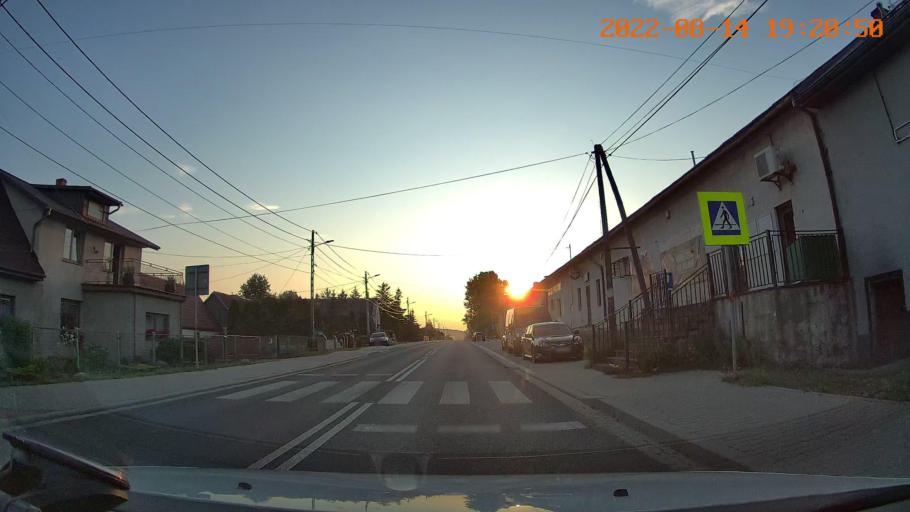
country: PL
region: Swietokrzyskie
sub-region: Powiat kielecki
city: Piekoszow
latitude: 50.8580
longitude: 20.5022
